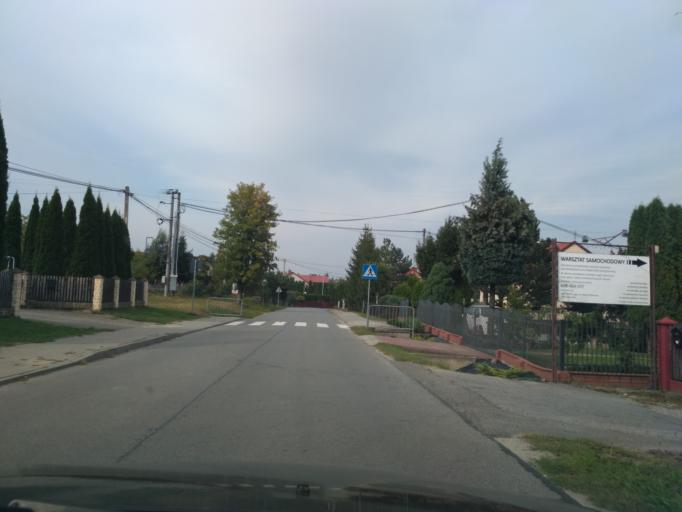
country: PL
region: Subcarpathian Voivodeship
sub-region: Powiat rzeszowski
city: Trzciana
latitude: 50.0615
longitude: 21.8348
